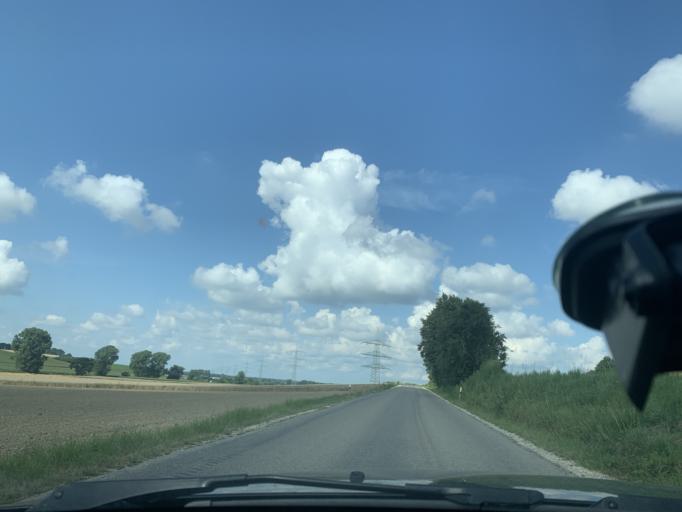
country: DE
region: Bavaria
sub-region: Swabia
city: Mering
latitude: 48.2902
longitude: 11.0032
